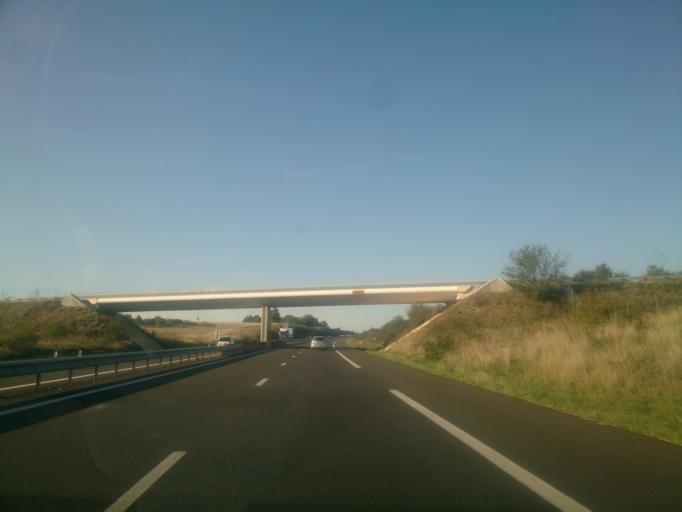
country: FR
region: Midi-Pyrenees
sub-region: Departement du Lot
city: Pradines
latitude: 44.5731
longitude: 1.5125
